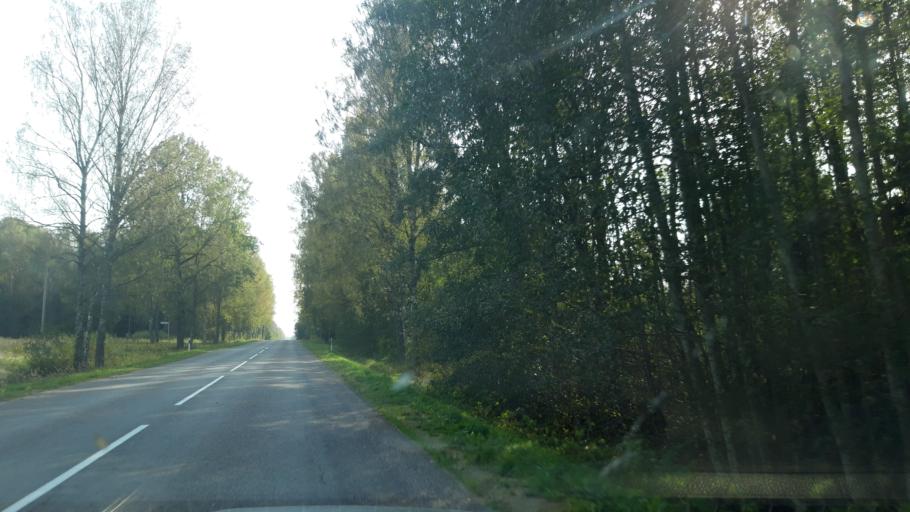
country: LV
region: Burtnieki
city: Matisi
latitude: 57.6543
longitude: 25.2319
